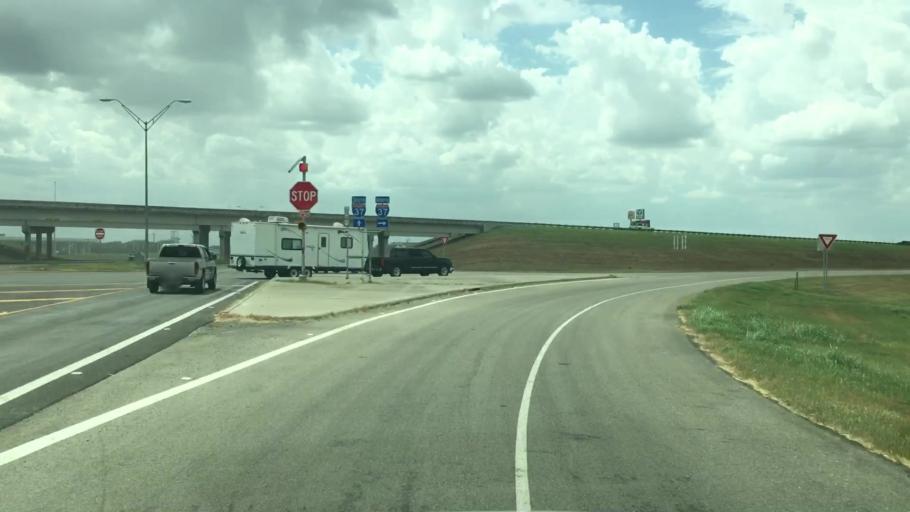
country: US
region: Texas
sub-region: Live Oak County
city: George West
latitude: 28.3379
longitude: -98.0253
